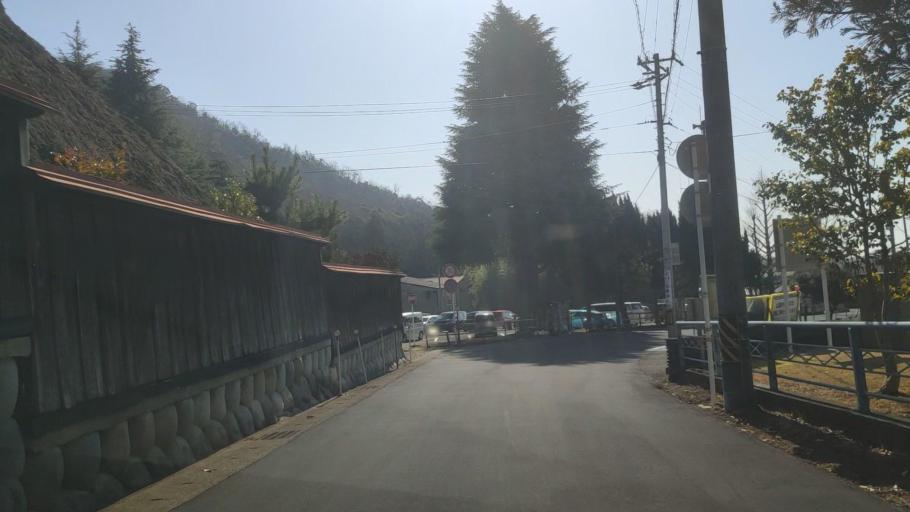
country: JP
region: Gifu
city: Gifu-shi
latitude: 35.4251
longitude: 136.7845
